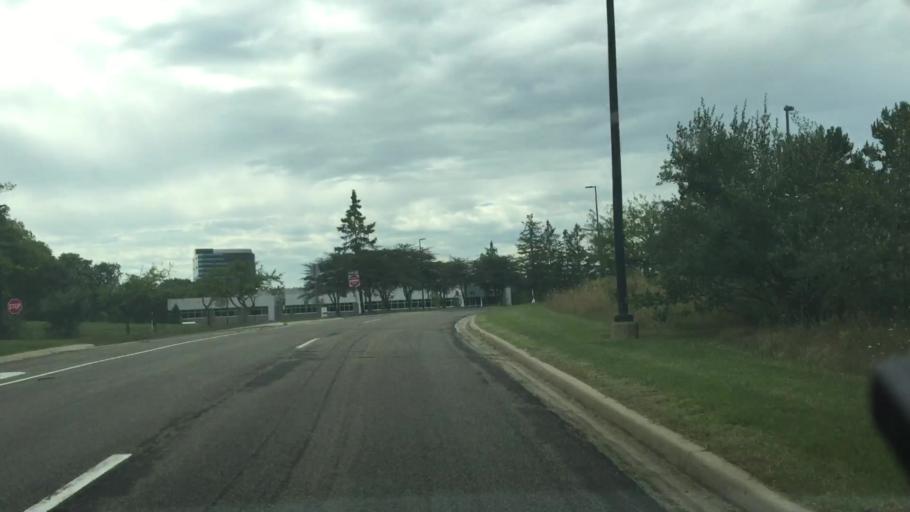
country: US
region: Michigan
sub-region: Oakland County
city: Auburn Hills
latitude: 42.6627
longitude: -83.2328
